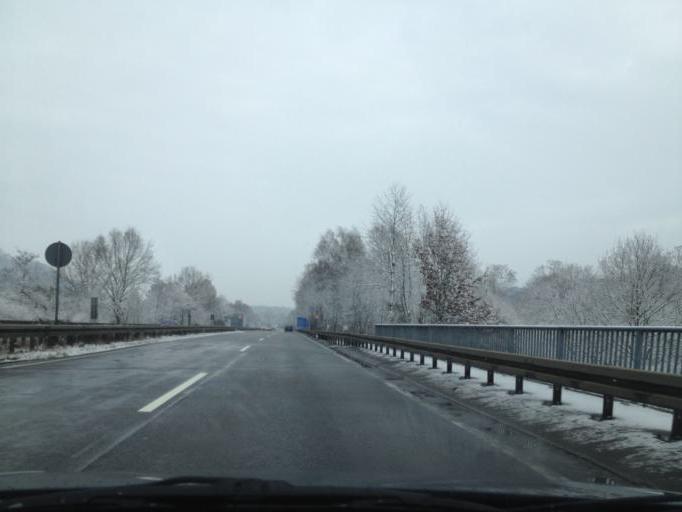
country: DE
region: Saarland
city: Homburg
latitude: 49.2746
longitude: 7.3109
